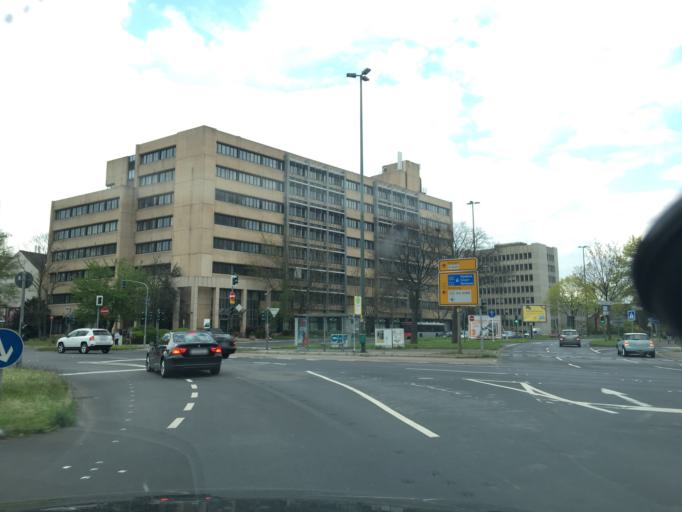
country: DE
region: North Rhine-Westphalia
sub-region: Regierungsbezirk Dusseldorf
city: Dusseldorf
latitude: 51.2501
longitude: 6.8022
